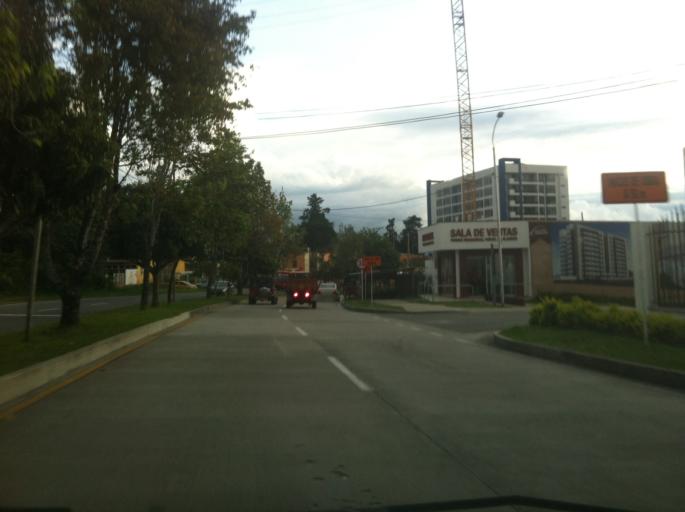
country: CO
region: Quindio
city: Calarca
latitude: 4.5688
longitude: -75.6510
